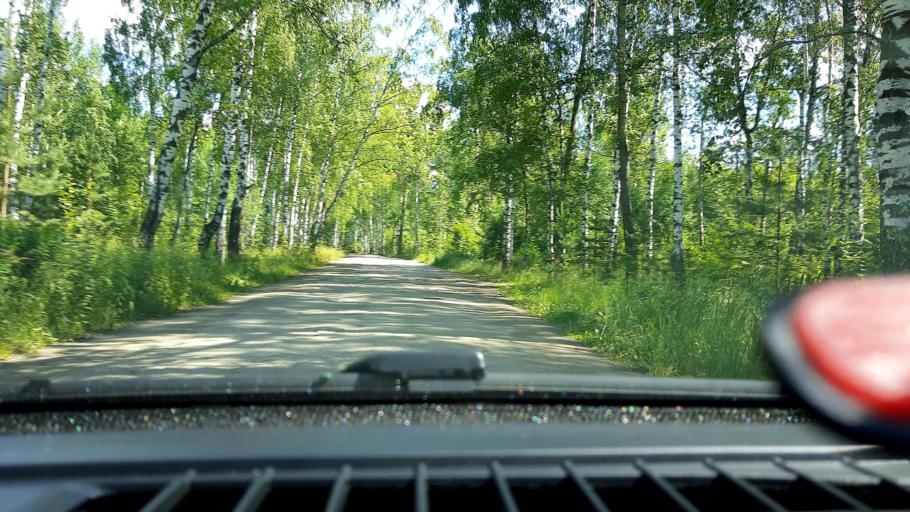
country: RU
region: Nizjnij Novgorod
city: Gorbatovka
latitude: 56.2953
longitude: 43.8161
